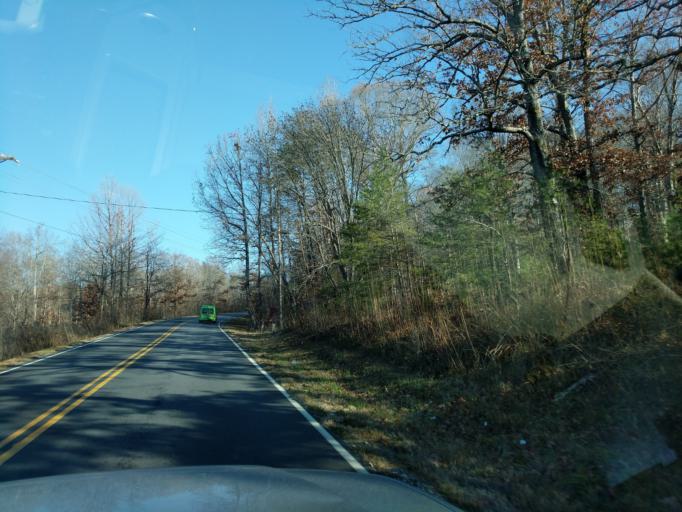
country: US
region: North Carolina
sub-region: Rutherford County
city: Rutherfordton
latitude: 35.2695
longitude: -82.0394
